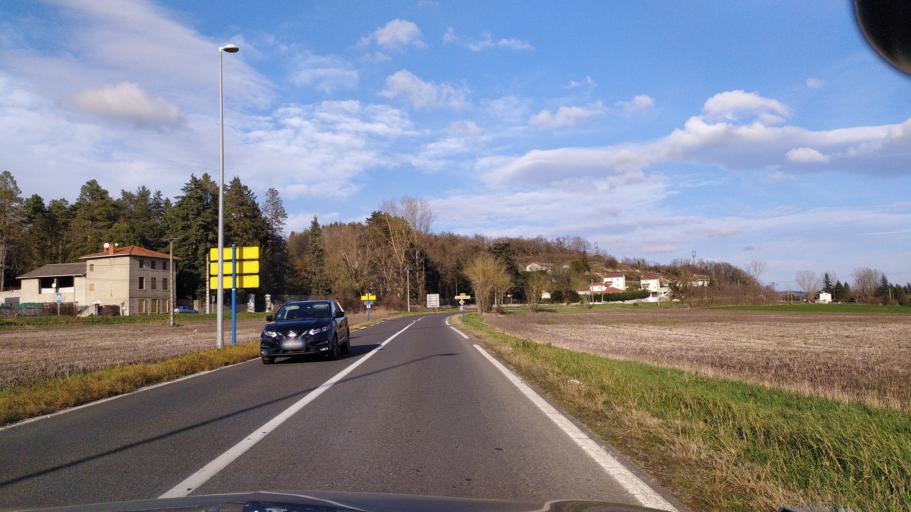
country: FR
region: Rhone-Alpes
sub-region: Departement de l'Isere
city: Pont-Eveque
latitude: 45.5358
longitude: 4.9066
